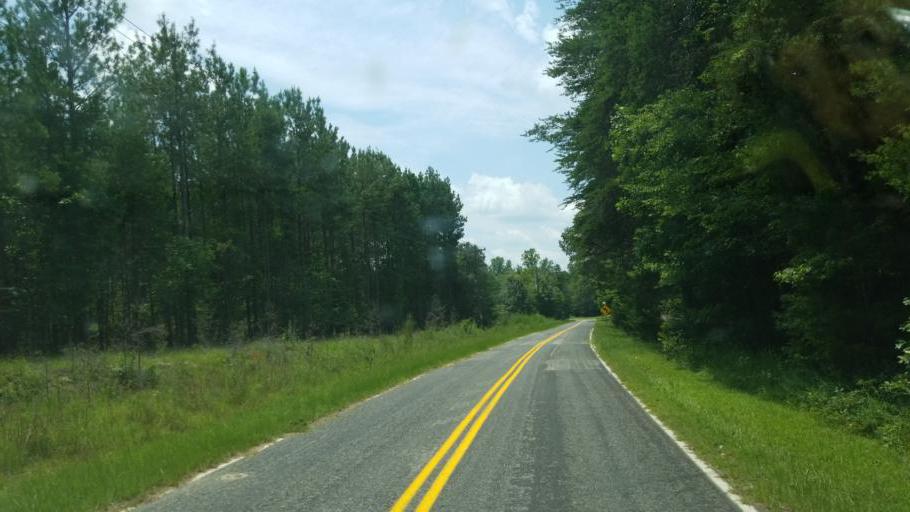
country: US
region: South Carolina
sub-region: Cherokee County
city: Blacksburg
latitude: 35.0883
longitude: -81.3995
